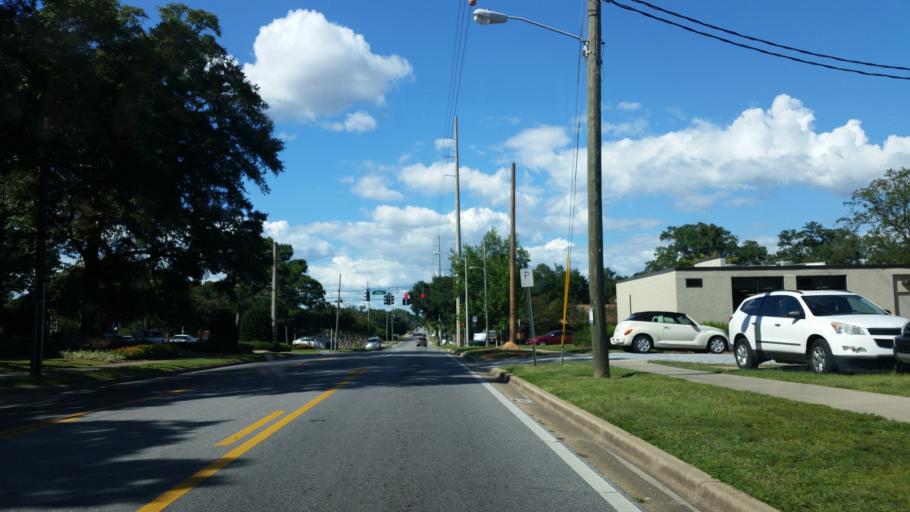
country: US
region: Florida
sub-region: Escambia County
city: Goulding
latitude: 30.4299
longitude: -87.2295
